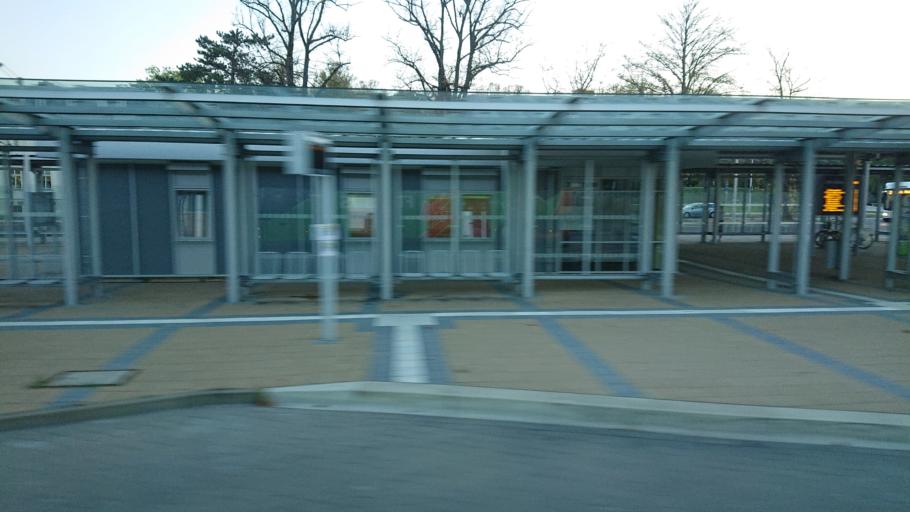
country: DE
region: Mecklenburg-Vorpommern
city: Greifswald
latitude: 54.0937
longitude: 13.3695
